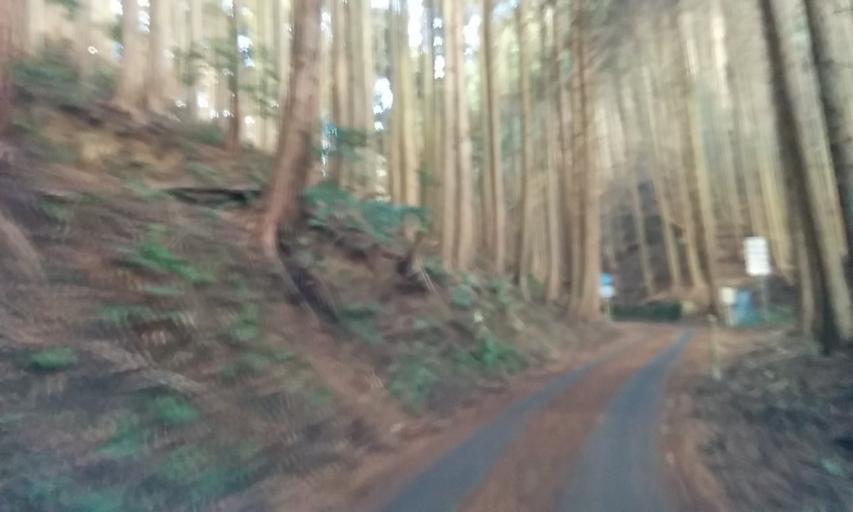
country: JP
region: Kyoto
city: Fukuchiyama
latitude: 35.2682
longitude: 135.0179
